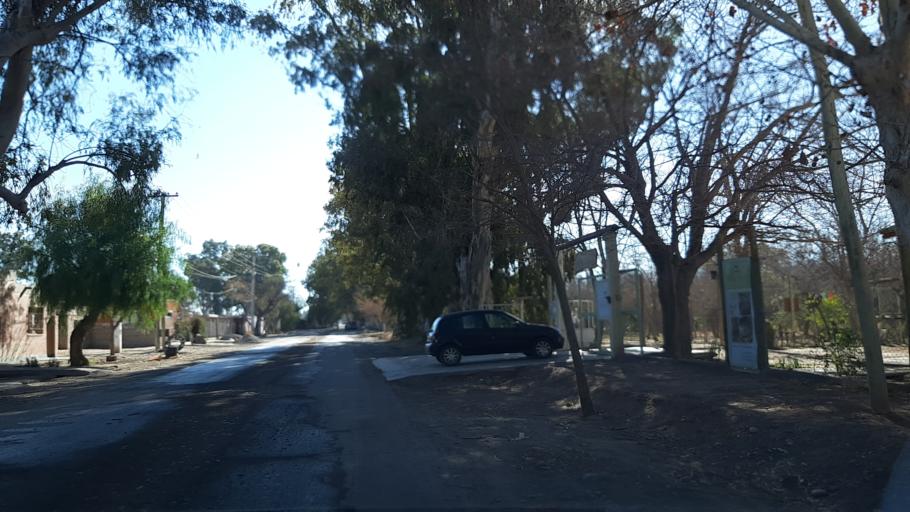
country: AR
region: San Juan
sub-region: Departamento de Zonda
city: Zonda
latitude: -31.5531
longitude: -68.7285
